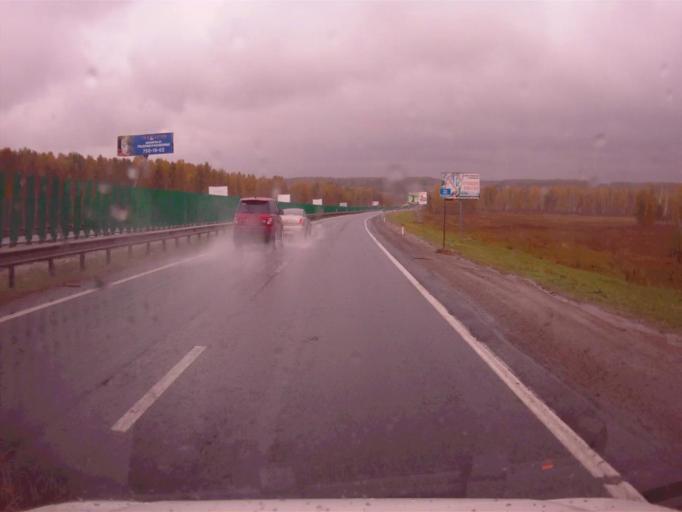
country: RU
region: Chelyabinsk
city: Dolgoderevenskoye
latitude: 55.3413
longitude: 61.3060
